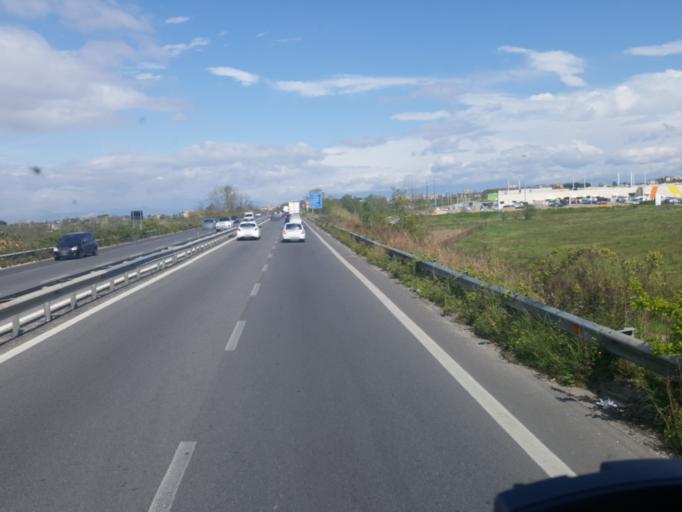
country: IT
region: Campania
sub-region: Provincia di Napoli
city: Qualiano
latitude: 40.9348
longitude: 14.1430
